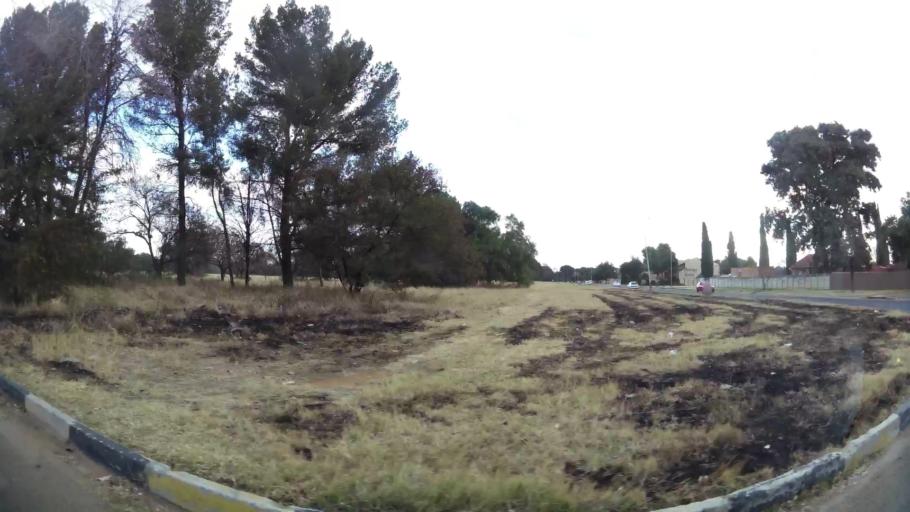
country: ZA
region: Orange Free State
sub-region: Lejweleputswa District Municipality
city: Welkom
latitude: -27.9952
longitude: 26.7178
